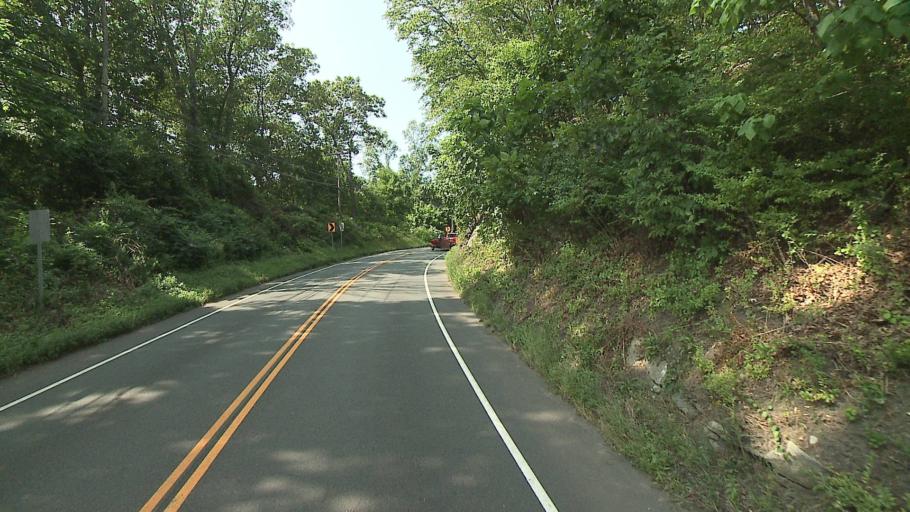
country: US
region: Connecticut
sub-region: Fairfield County
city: Newtown
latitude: 41.3568
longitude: -73.2635
